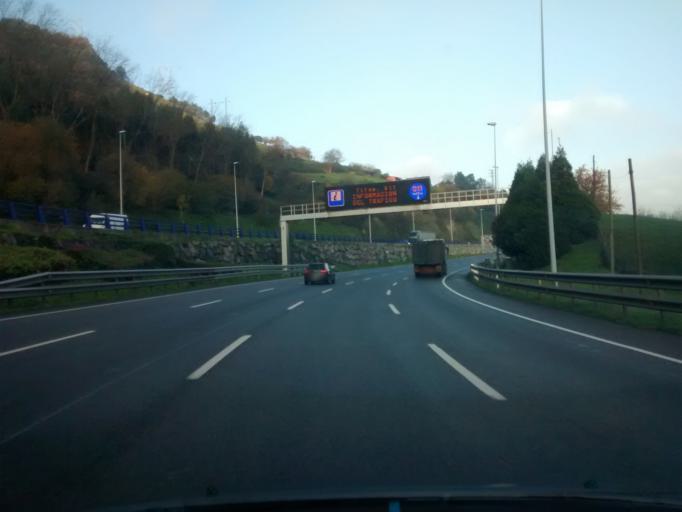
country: ES
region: Basque Country
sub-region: Bizkaia
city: Santutxu
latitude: 43.2388
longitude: -2.9250
